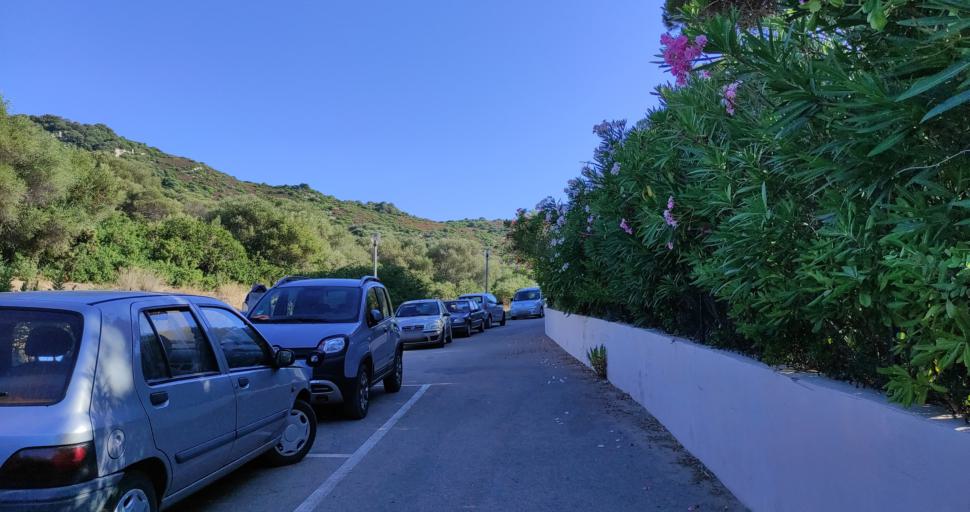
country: FR
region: Corsica
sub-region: Departement de la Corse-du-Sud
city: Alata
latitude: 41.9943
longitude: 8.6669
